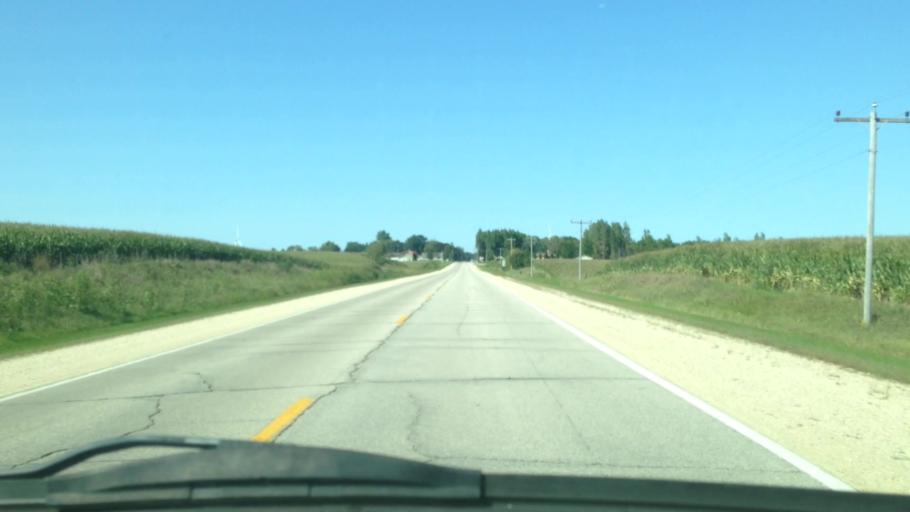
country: US
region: Minnesota
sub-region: Winona County
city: Lewiston
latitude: 43.9704
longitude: -91.8692
